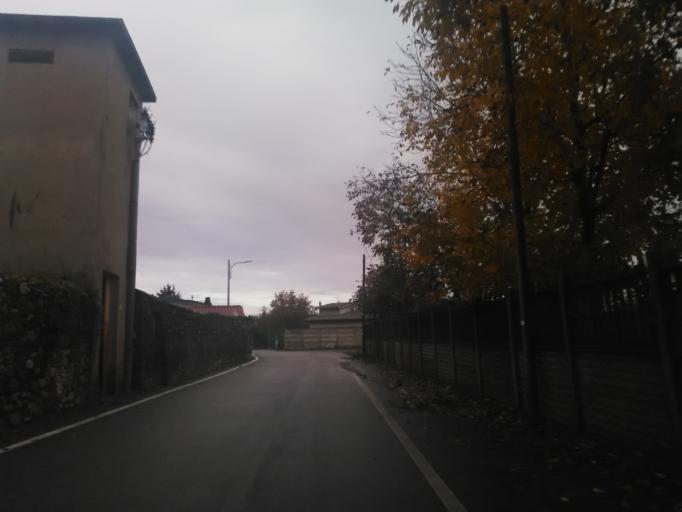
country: IT
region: Piedmont
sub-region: Provincia di Vercelli
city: Gattinara
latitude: 45.6121
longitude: 8.3753
